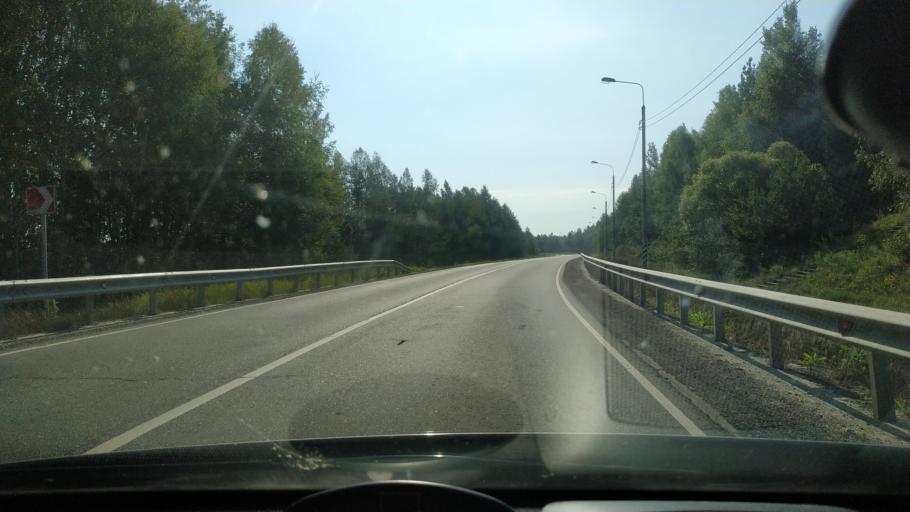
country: RU
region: Moskovskaya
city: Dmitrovskiy Pogost
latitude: 55.2290
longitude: 39.9230
